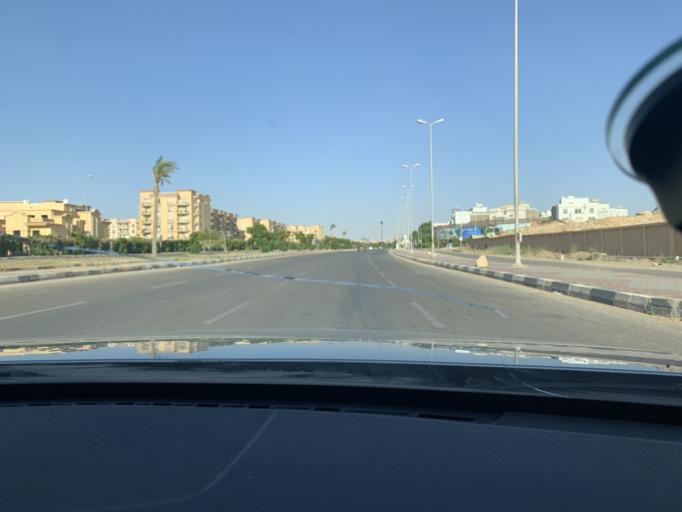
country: EG
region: Muhafazat al Qalyubiyah
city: Al Khankah
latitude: 30.0529
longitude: 31.5039
